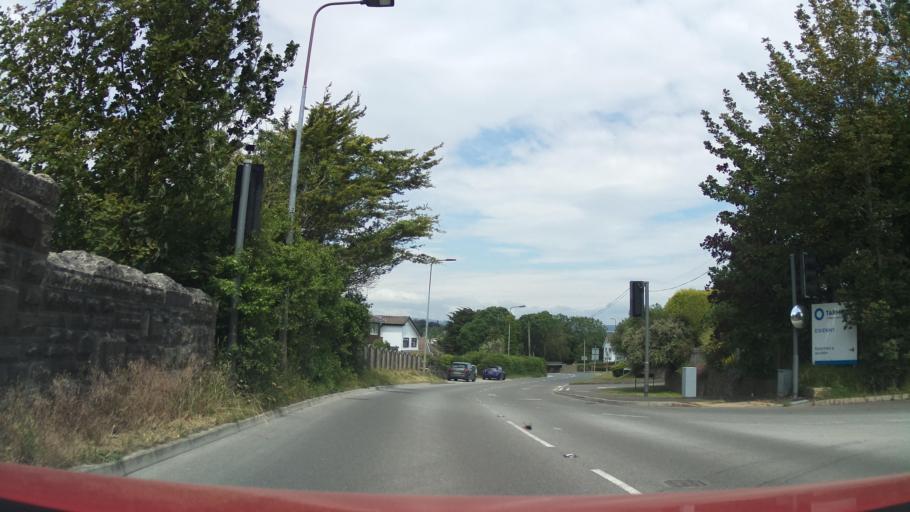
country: GB
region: Wales
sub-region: Bridgend county borough
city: Merthyr Mawr
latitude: 51.4811
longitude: -3.5846
